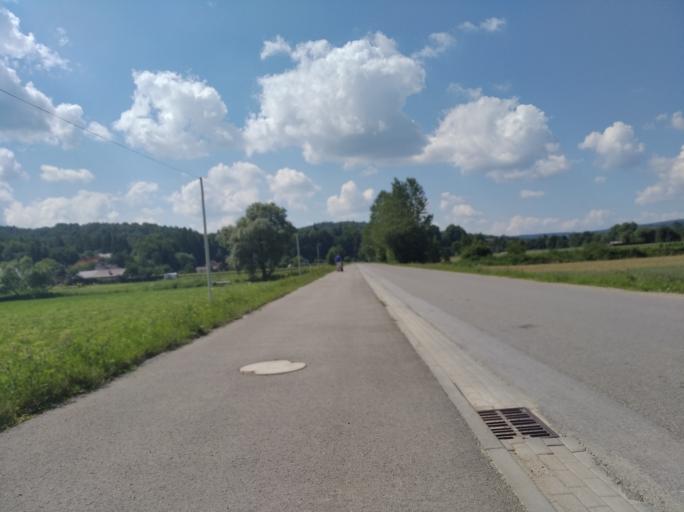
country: PL
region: Subcarpathian Voivodeship
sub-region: Powiat rzeszowski
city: Dynow
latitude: 49.7872
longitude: 22.2389
